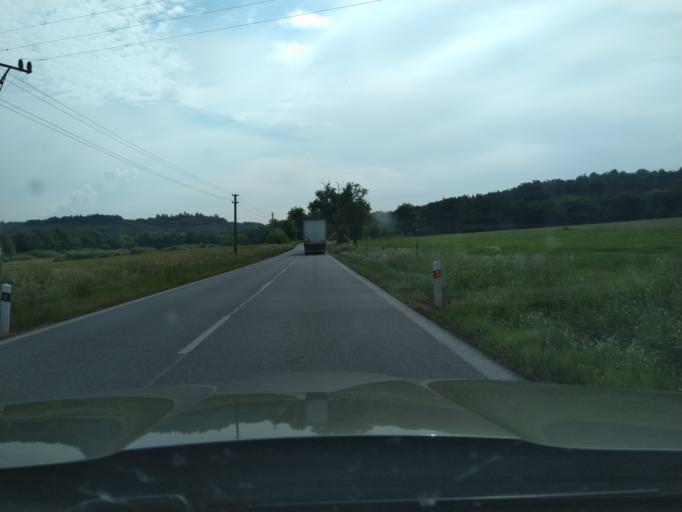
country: CZ
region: Jihocesky
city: Netolice
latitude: 49.0560
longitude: 14.1571
